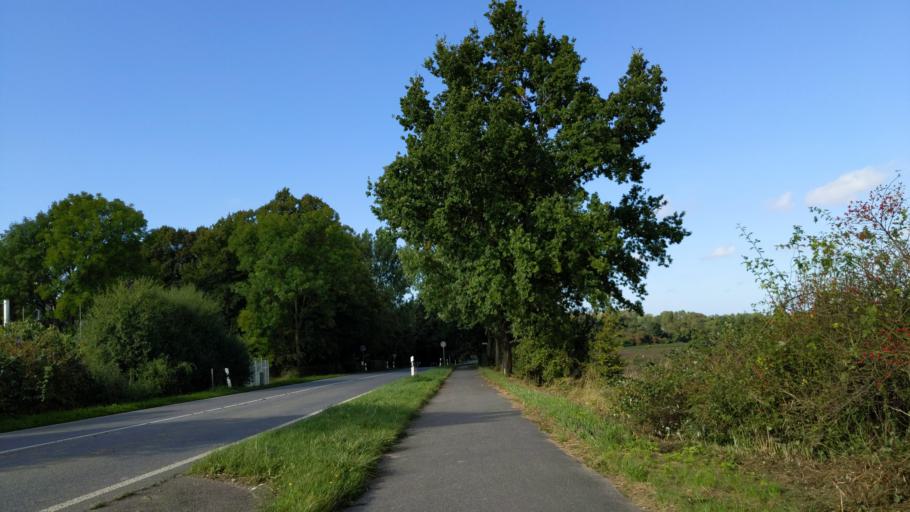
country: DE
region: Schleswig-Holstein
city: Stockelsdorf
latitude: 53.9437
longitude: 10.6282
